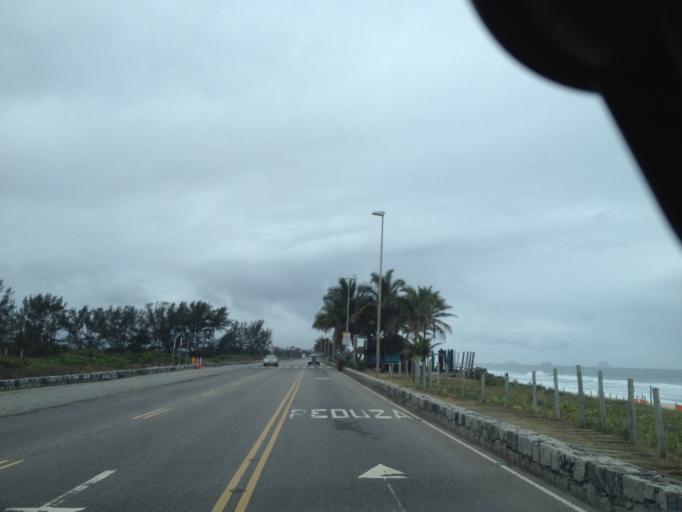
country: BR
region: Rio de Janeiro
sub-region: Nilopolis
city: Nilopolis
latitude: -23.0202
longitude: -43.4379
